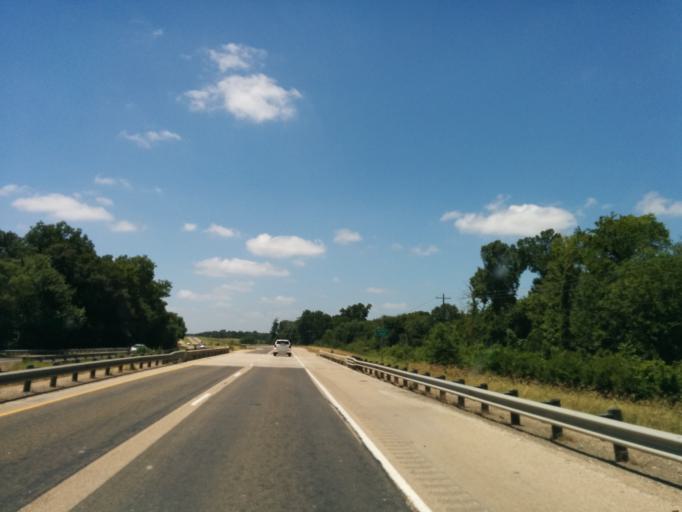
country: US
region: Texas
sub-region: Brazos County
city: Bryan
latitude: 30.7441
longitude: -96.3141
